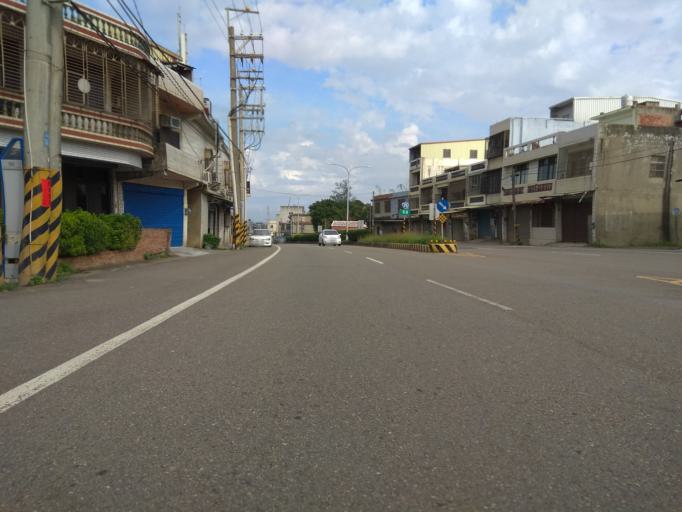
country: TW
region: Taiwan
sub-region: Hsinchu
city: Zhubei
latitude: 24.9752
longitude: 121.0269
